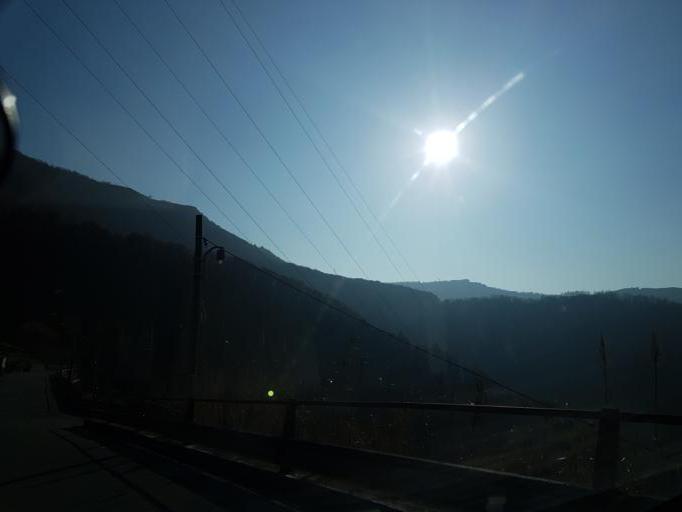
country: IT
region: Liguria
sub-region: Provincia di Genova
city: Manesseno
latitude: 44.4597
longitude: 8.9192
